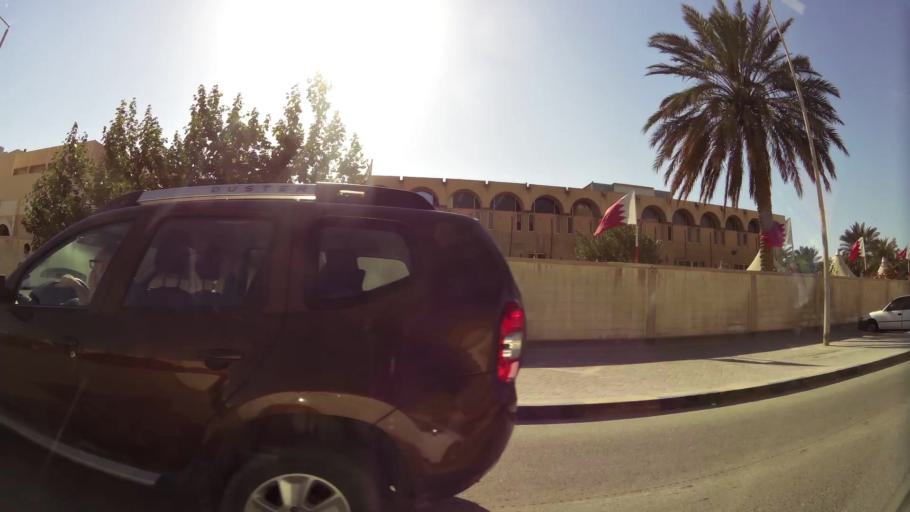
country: BH
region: Manama
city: Manama
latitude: 26.2175
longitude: 50.5743
